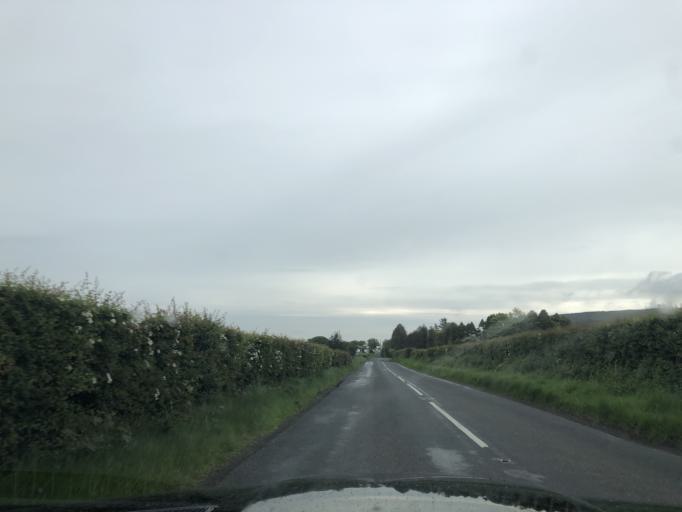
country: GB
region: Northern Ireland
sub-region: Down District
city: Castlewellan
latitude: 54.2179
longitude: -6.0271
